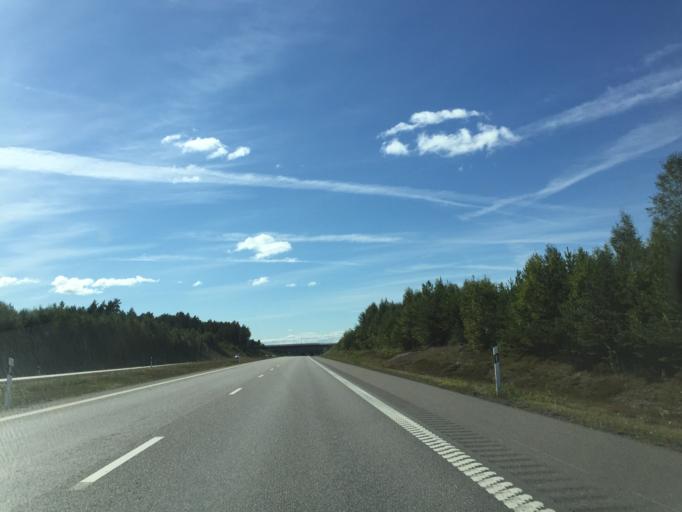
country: SE
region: OErebro
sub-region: Lindesbergs Kommun
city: Fellingsbro
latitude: 59.3873
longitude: 15.6774
